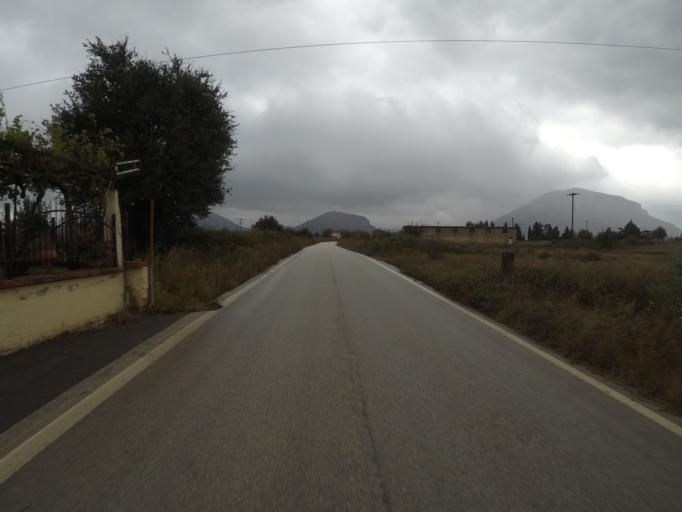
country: GR
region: Peloponnese
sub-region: Nomos Arkadias
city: Tripoli
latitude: 37.5761
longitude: 22.4135
